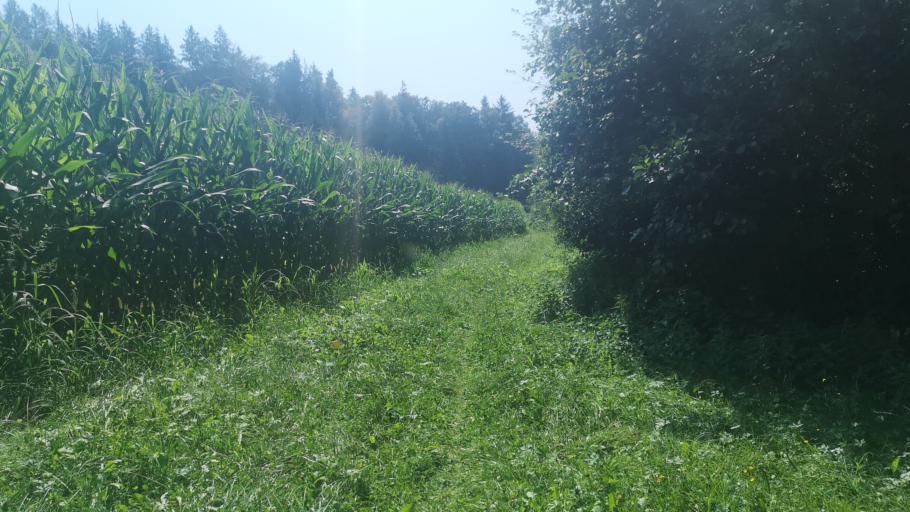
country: AT
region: Styria
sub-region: Politischer Bezirk Deutschlandsberg
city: Lannach
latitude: 46.9396
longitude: 15.3371
